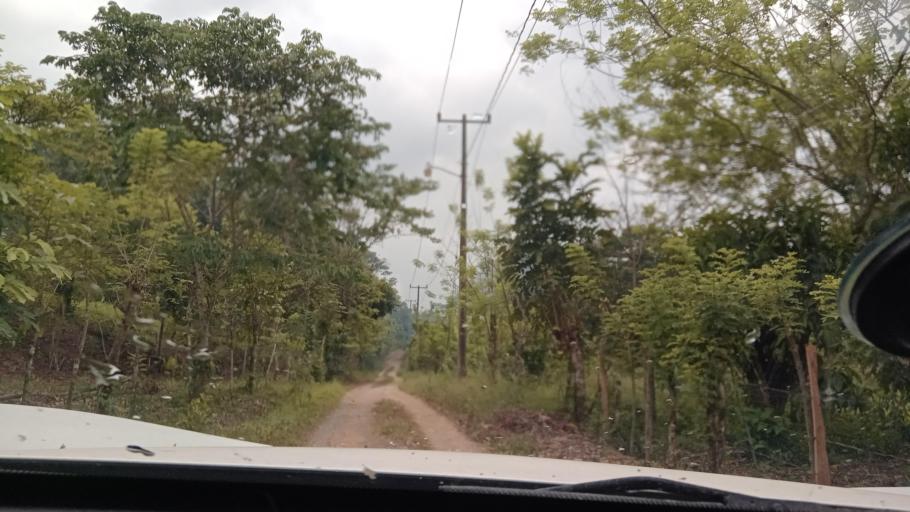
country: MX
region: Veracruz
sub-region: Uxpanapa
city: Poblado 10
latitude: 17.4506
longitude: -94.0901
